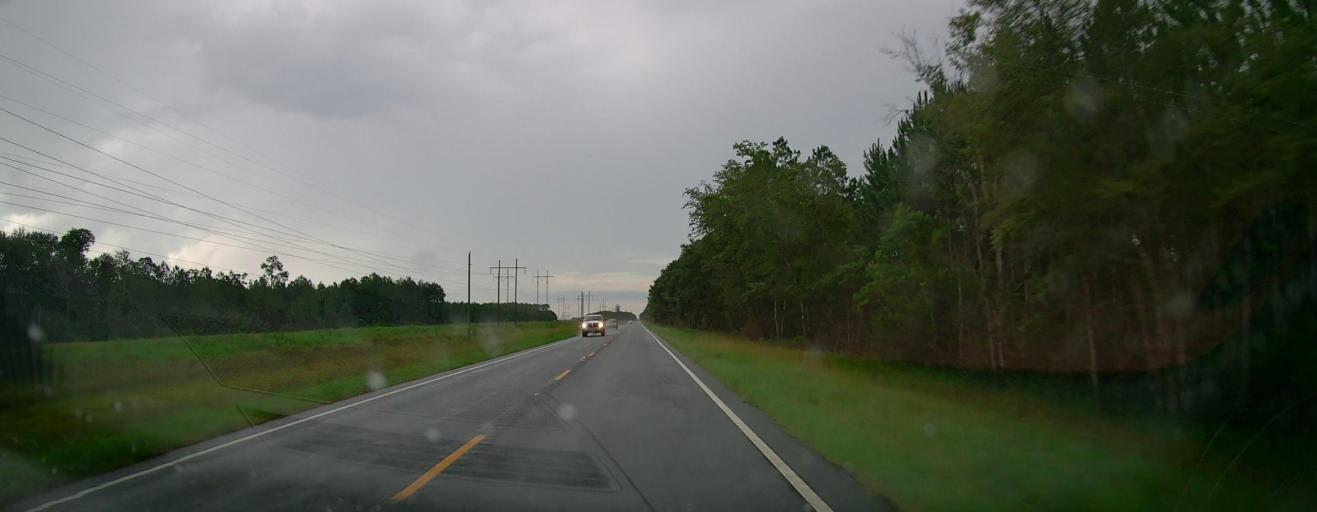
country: US
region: Georgia
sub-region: Brantley County
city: Nahunta
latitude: 31.3389
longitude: -81.8524
